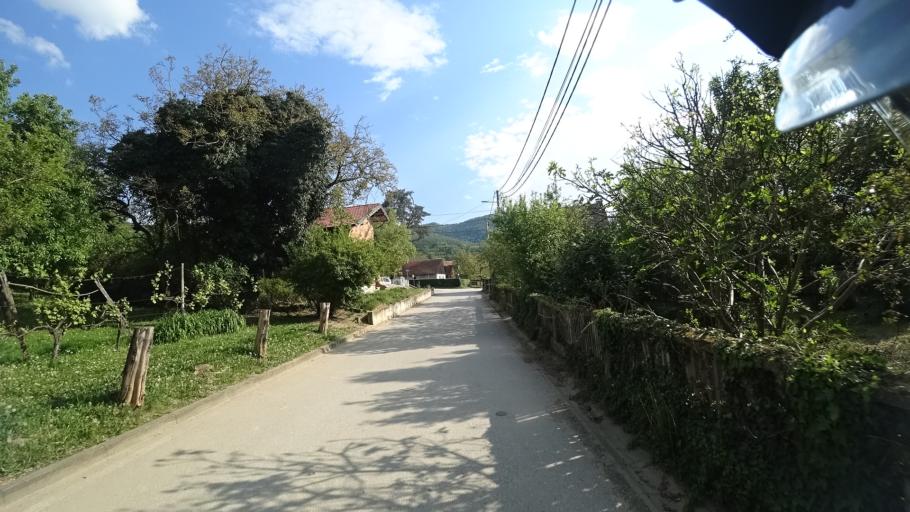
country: HR
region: Zagrebacka
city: Jablanovec
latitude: 45.8851
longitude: 15.8639
